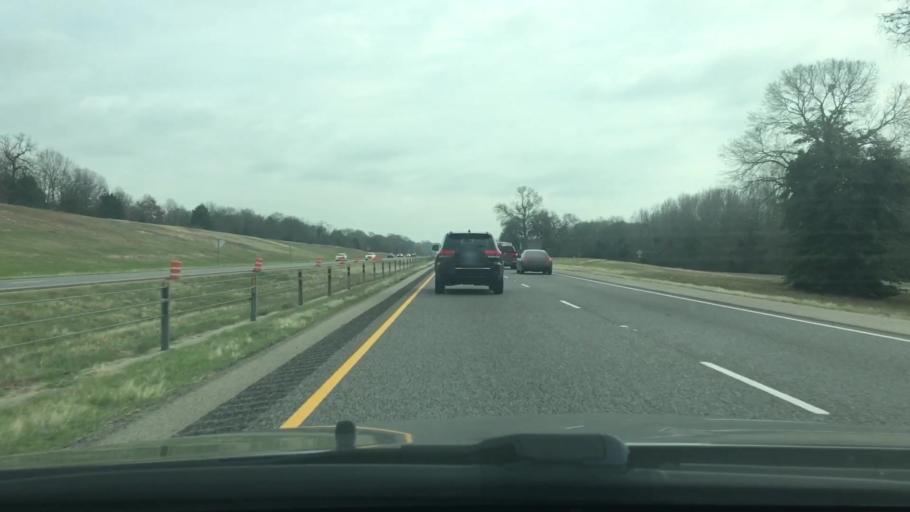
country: US
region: Texas
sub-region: Leon County
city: Buffalo
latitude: 31.4973
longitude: -96.0964
